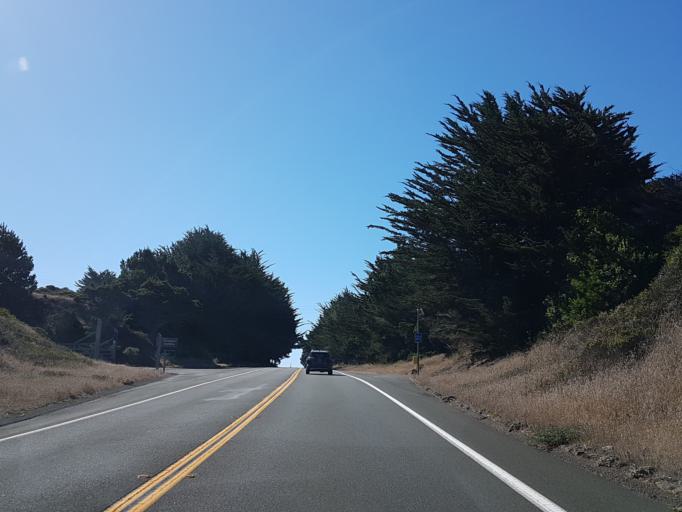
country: US
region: California
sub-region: Mendocino County
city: Boonville
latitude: 39.0315
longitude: -123.6882
